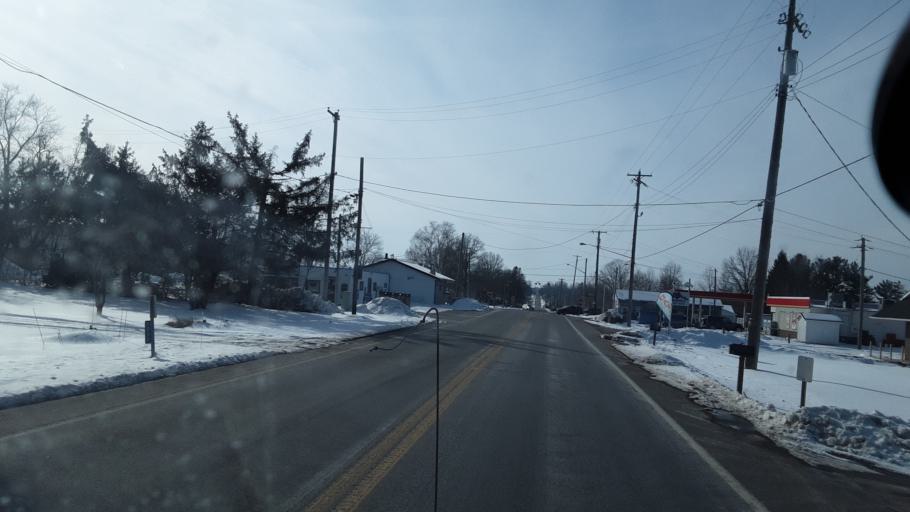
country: US
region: Ohio
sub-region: Stark County
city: Alliance
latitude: 41.0237
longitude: -81.1463
